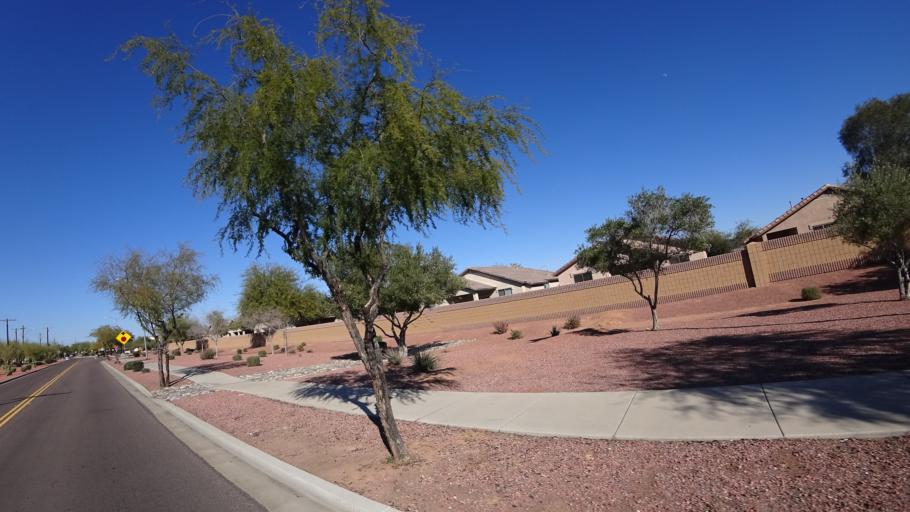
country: US
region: Arizona
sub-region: Maricopa County
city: Sun City West
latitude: 33.6479
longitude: -112.4267
